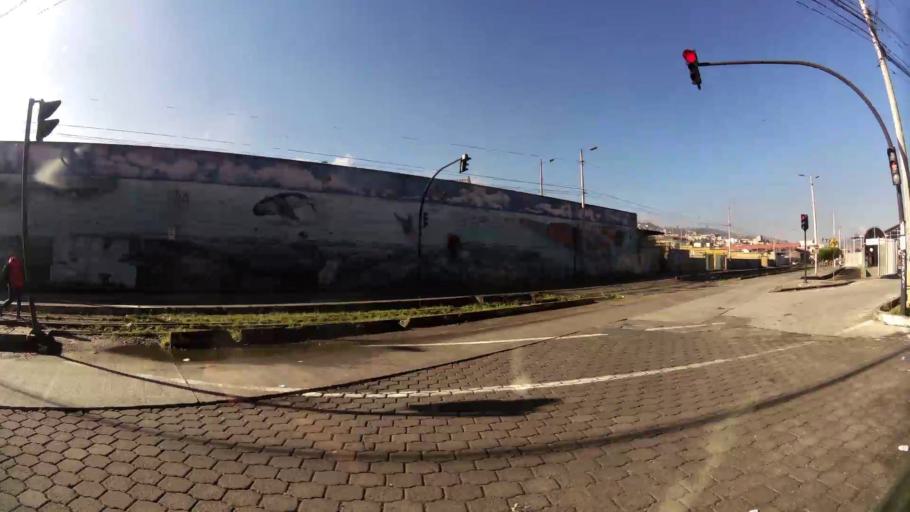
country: EC
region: Pichincha
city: Quito
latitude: -0.2483
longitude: -78.5190
